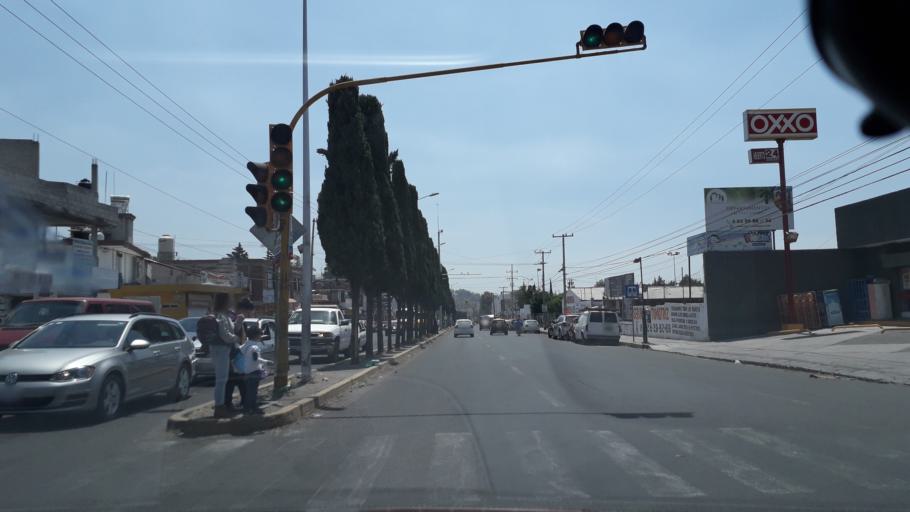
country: MX
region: Puebla
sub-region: Amozoc
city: Casa Blanca
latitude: 19.0653
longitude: -98.1216
